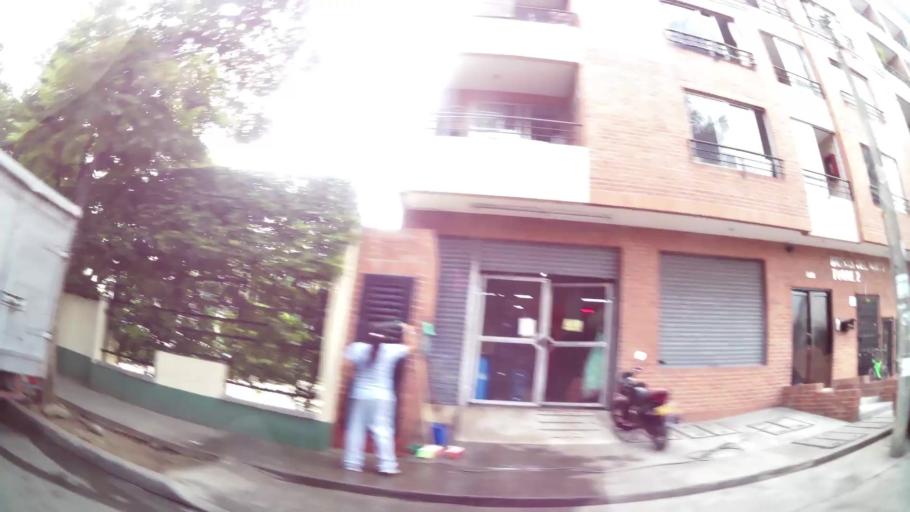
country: CO
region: Valle del Cauca
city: Cali
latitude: 3.4809
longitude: -76.4976
